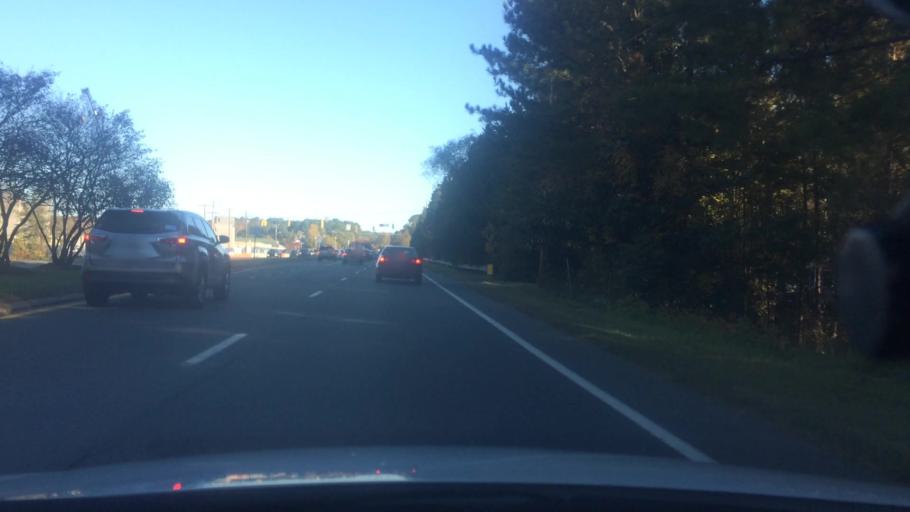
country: US
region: North Carolina
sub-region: Orange County
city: Chapel Hill
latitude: 35.9312
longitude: -79.0240
